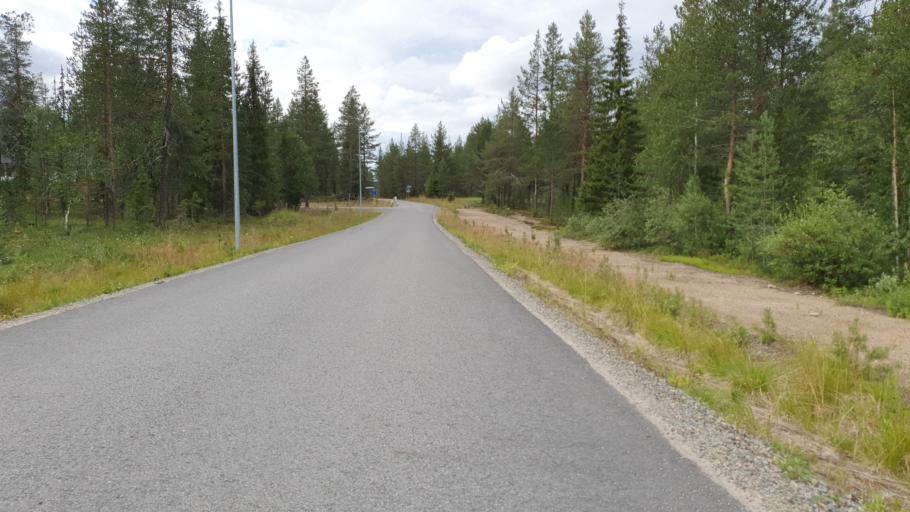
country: FI
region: Lapland
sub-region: Tunturi-Lappi
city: Kolari
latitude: 67.5981
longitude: 24.1385
